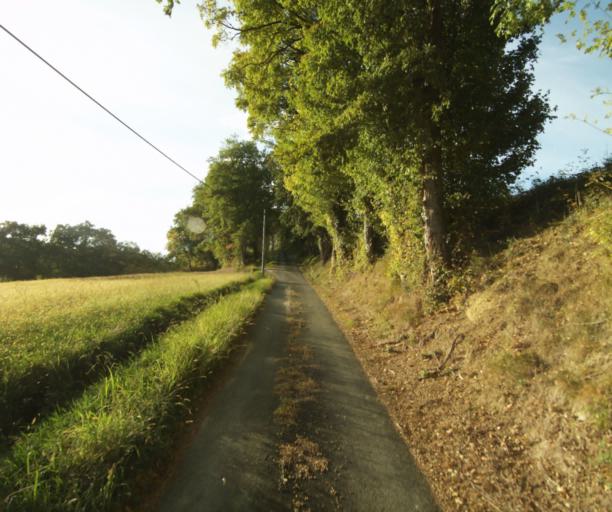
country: FR
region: Midi-Pyrenees
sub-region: Departement du Gers
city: Gondrin
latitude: 43.8850
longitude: 0.2702
